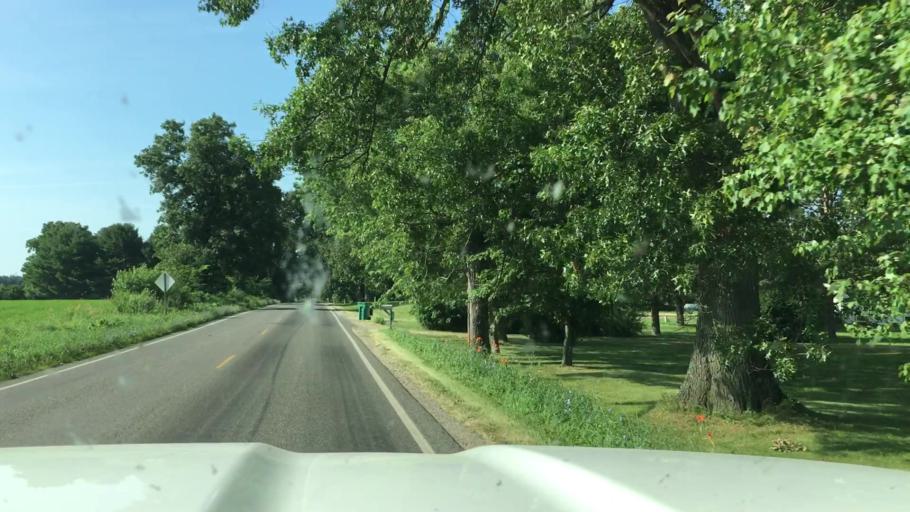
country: US
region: Michigan
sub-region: Barry County
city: Stony Point
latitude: 42.4554
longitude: -85.4549
